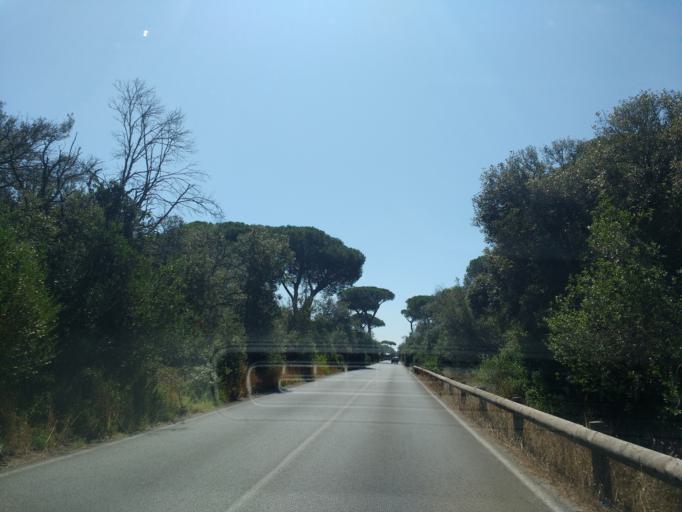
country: IT
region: Latium
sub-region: Citta metropolitana di Roma Capitale
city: Acilia-Castel Fusano-Ostia Antica
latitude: 41.7208
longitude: 12.3475
